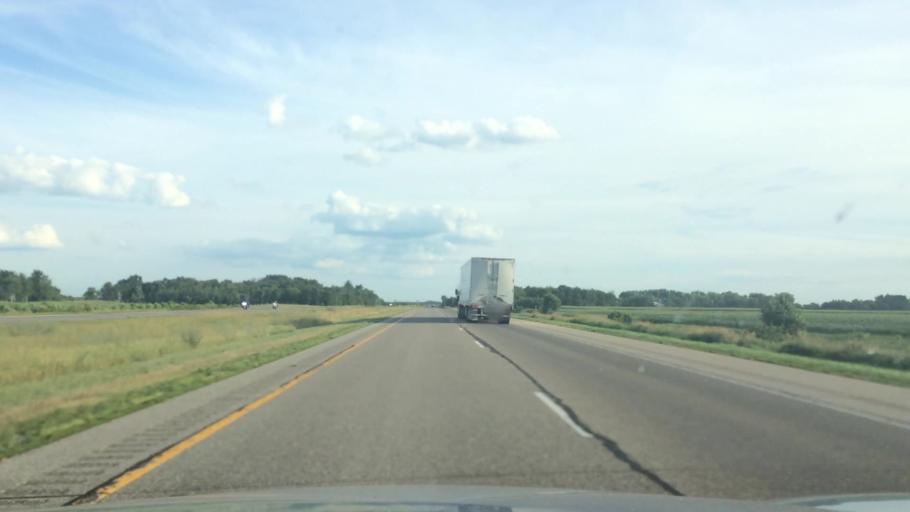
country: US
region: Wisconsin
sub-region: Portage County
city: Plover
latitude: 44.3824
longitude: -89.5200
